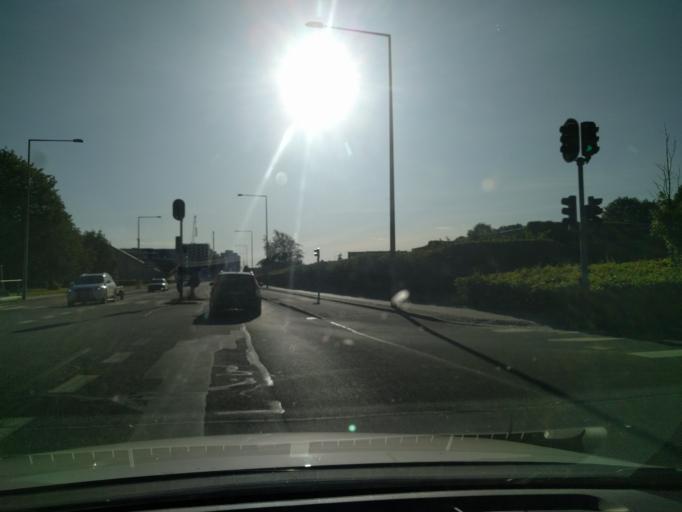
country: DK
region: Central Jutland
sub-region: Horsens Kommune
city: Horsens
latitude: 55.8611
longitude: 9.8717
